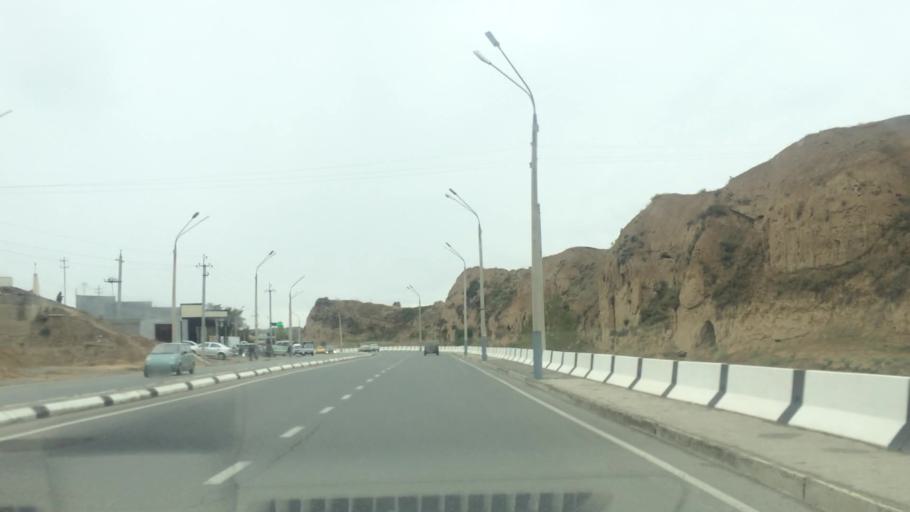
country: UZ
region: Samarqand
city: Samarqand
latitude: 39.6673
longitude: 66.9948
